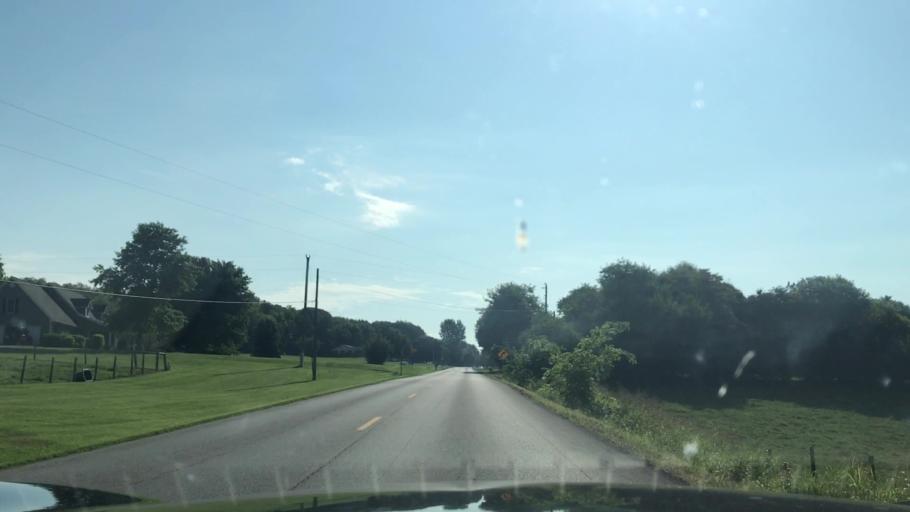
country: US
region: Kentucky
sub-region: Hart County
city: Horse Cave
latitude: 37.1672
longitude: -85.8248
